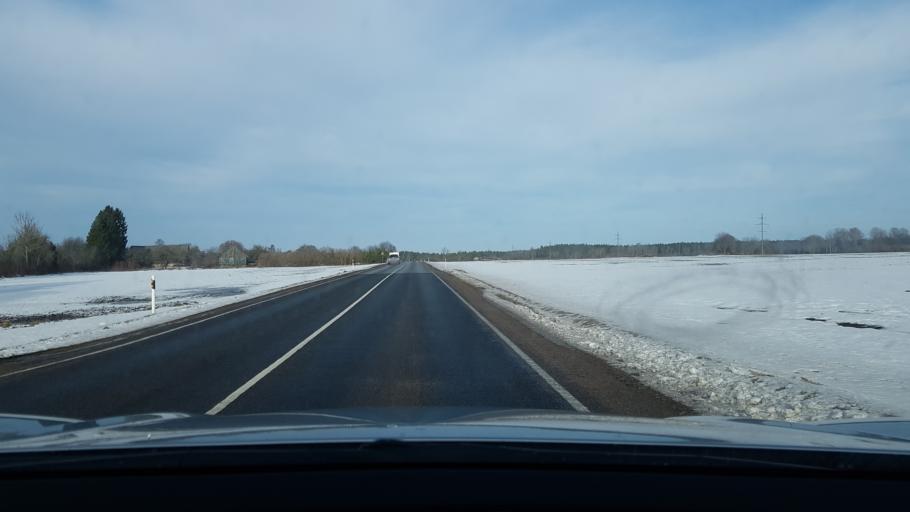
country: EE
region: Saare
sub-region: Kuressaare linn
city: Kuressaare
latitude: 58.3092
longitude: 22.5417
